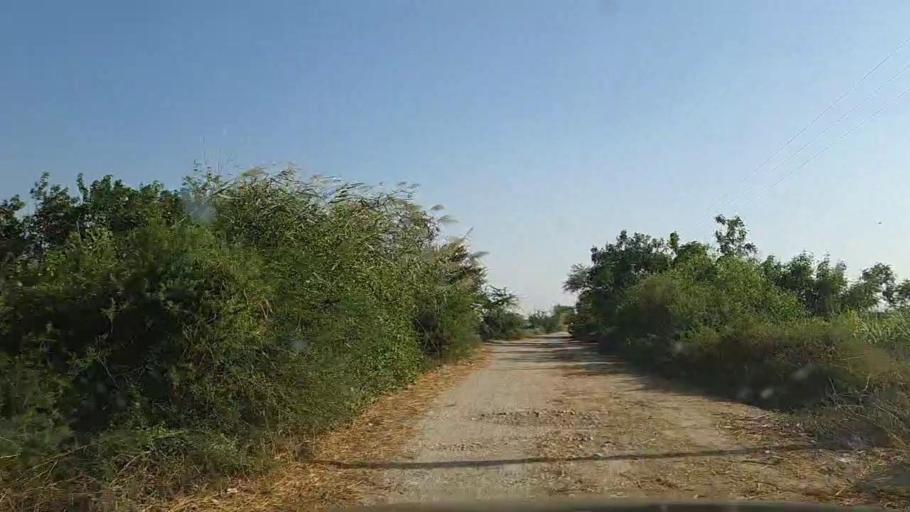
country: PK
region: Sindh
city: Daro Mehar
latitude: 24.6320
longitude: 68.0781
